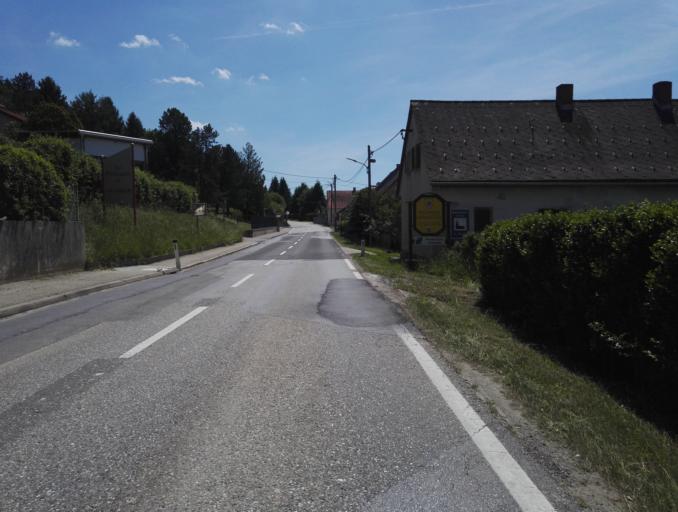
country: AT
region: Styria
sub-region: Politischer Bezirk Graz-Umgebung
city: Grambach
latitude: 47.0051
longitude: 15.5036
